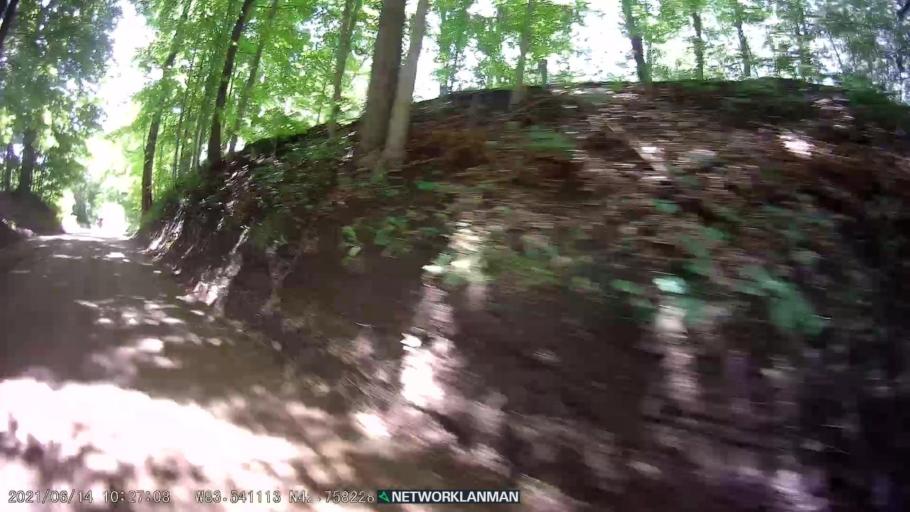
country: US
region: Michigan
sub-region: Oakland County
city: Holly
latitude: 42.7582
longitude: -83.5412
